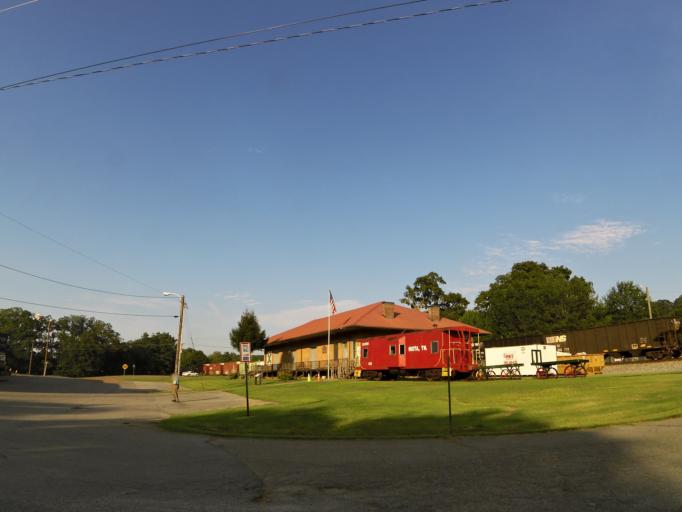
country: US
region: Tennessee
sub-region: McMinn County
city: Athens
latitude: 35.5149
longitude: -84.5467
